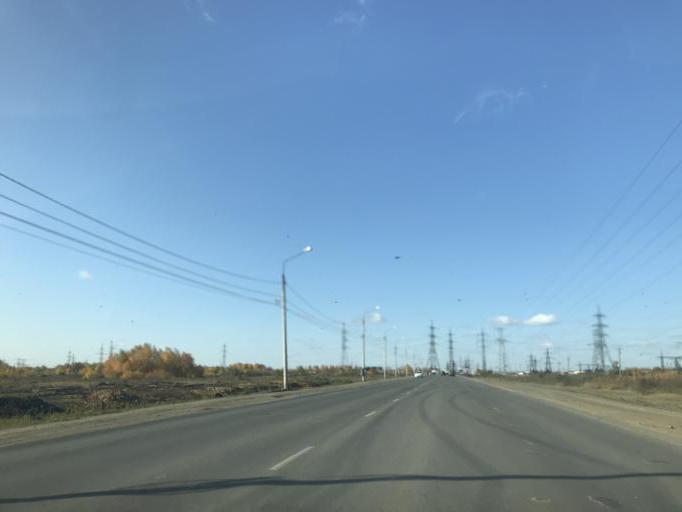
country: RU
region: Chelyabinsk
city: Roshchino
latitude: 55.2223
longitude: 61.2945
